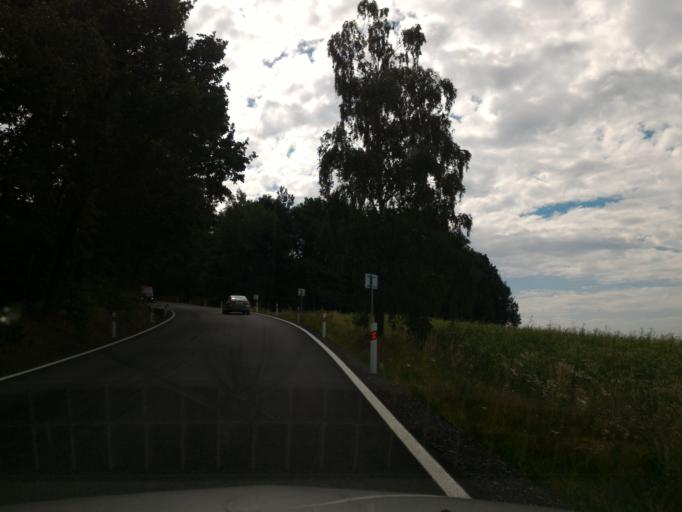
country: CZ
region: Vysocina
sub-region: Okres Jihlava
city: Telc
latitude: 49.1603
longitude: 15.5111
